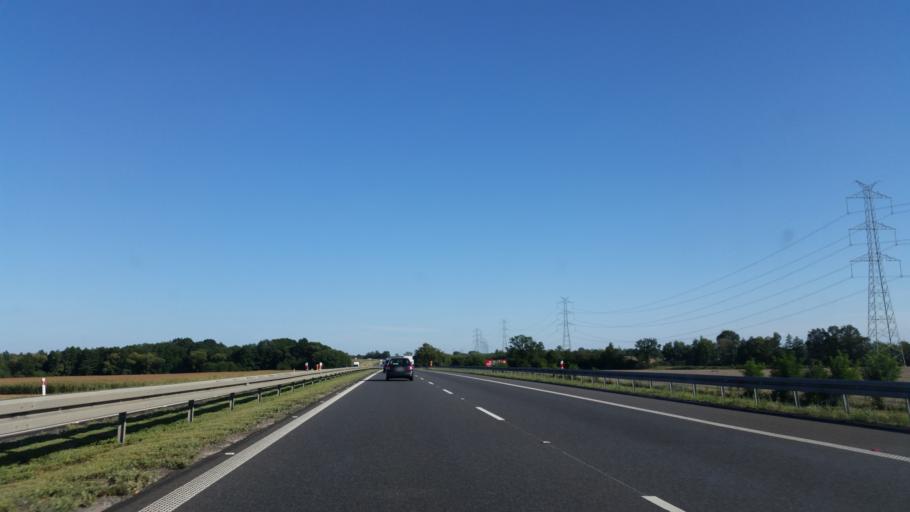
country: PL
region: Lower Silesian Voivodeship
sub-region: Powiat strzelinski
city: Wiazow
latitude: 50.8259
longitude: 17.2958
